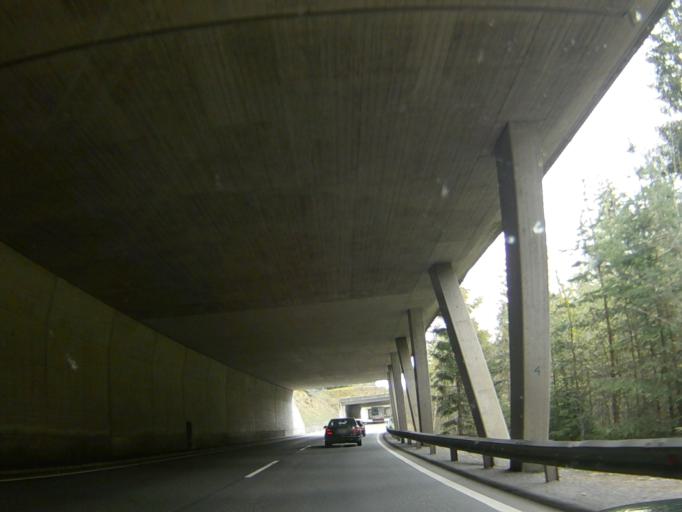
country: AT
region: Tyrol
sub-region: Politischer Bezirk Landeck
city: Nauders
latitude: 46.9297
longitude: 10.4947
